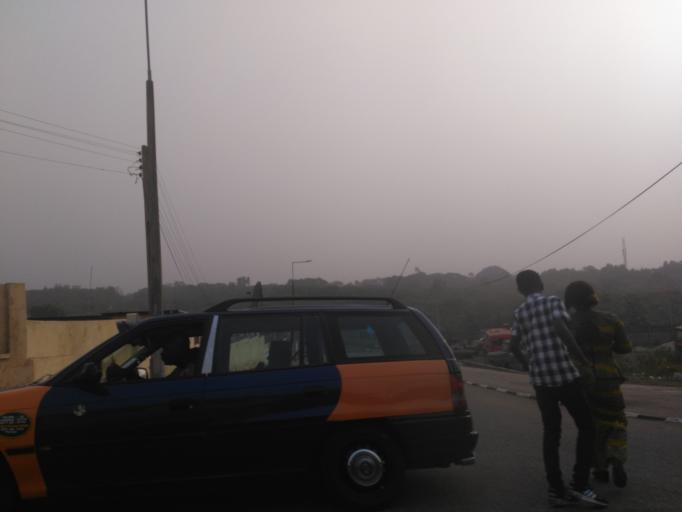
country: GH
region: Ashanti
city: Kumasi
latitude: 6.7096
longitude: -1.6133
